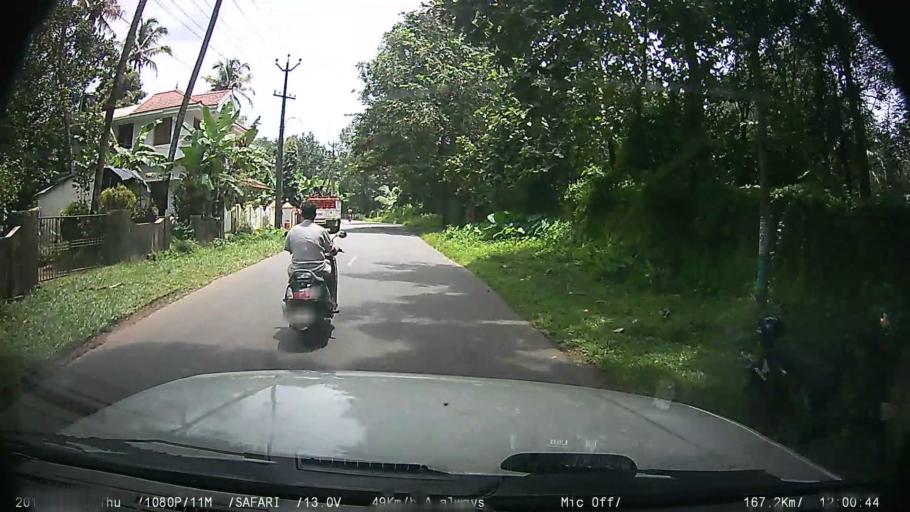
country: IN
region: Kerala
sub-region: Ernakulam
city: Kotamangalam
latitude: 10.1042
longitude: 76.6641
